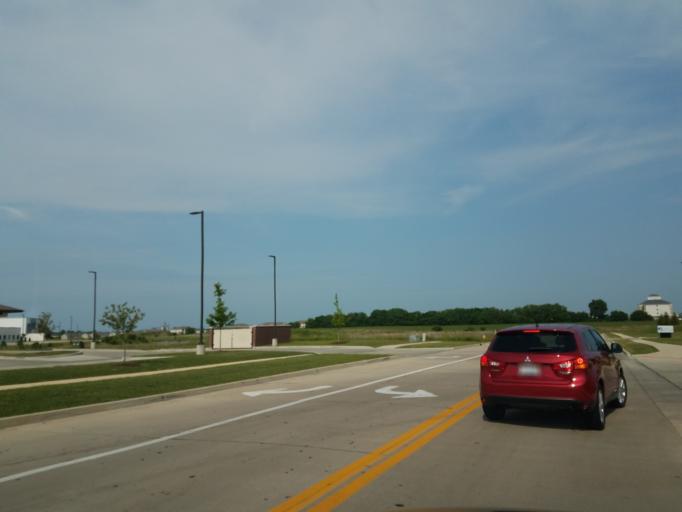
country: US
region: Illinois
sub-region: McLean County
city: Bloomington
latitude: 40.4894
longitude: -88.9189
